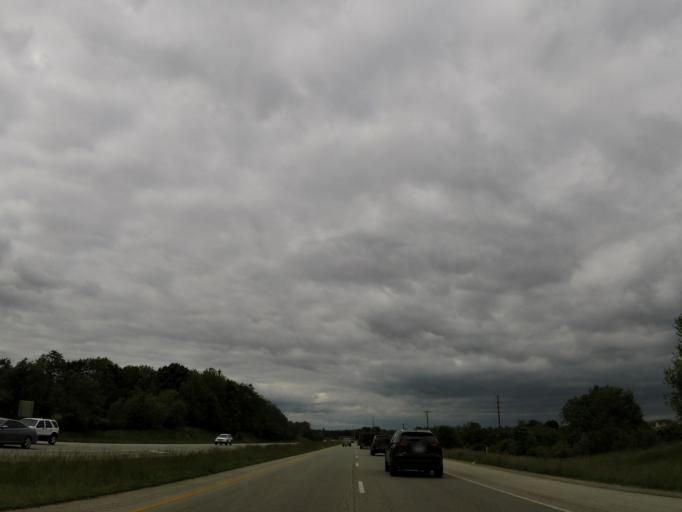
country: US
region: Kentucky
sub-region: Scott County
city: Georgetown
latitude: 38.1989
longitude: -84.5384
